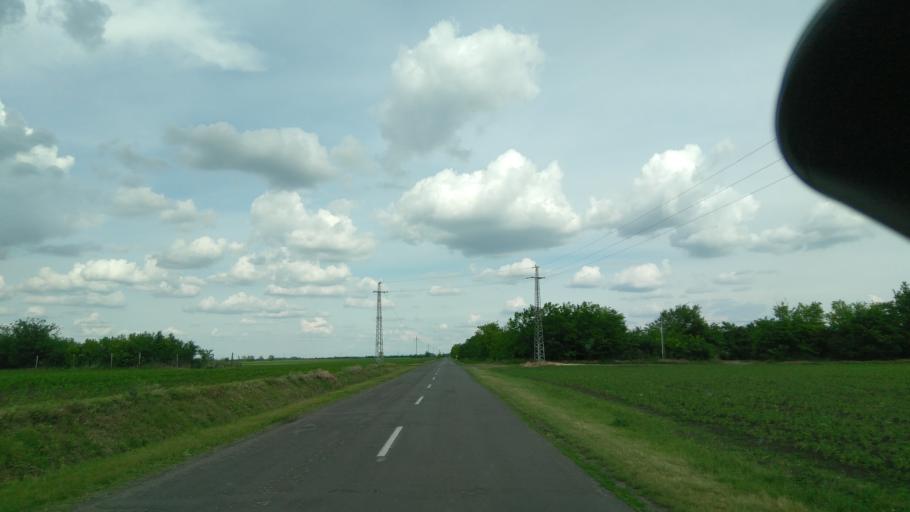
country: RO
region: Arad
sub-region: Comuna Peregu Mare
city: Peregu Mic
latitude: 46.3015
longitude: 20.9255
